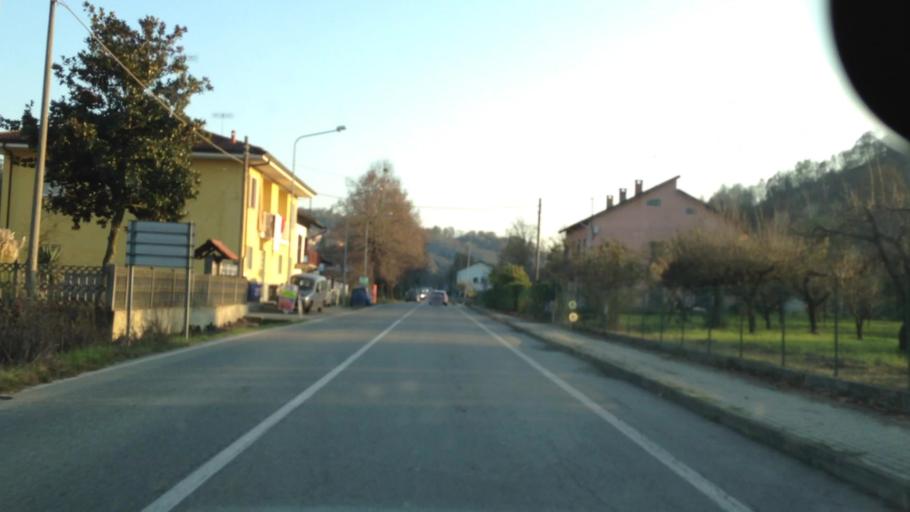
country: IT
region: Piedmont
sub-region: Provincia di Torino
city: Cavagnolo
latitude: 45.1503
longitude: 8.0528
